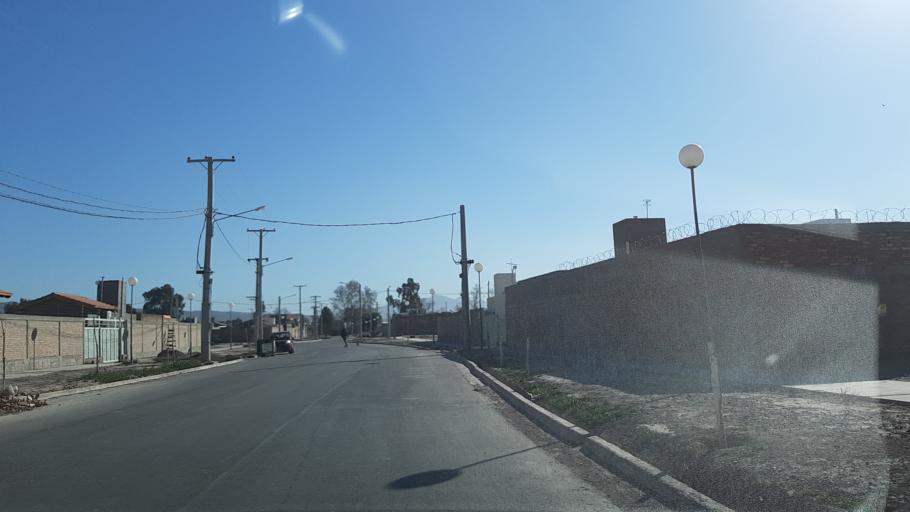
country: AR
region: San Juan
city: San Juan
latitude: -31.5184
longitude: -68.5911
